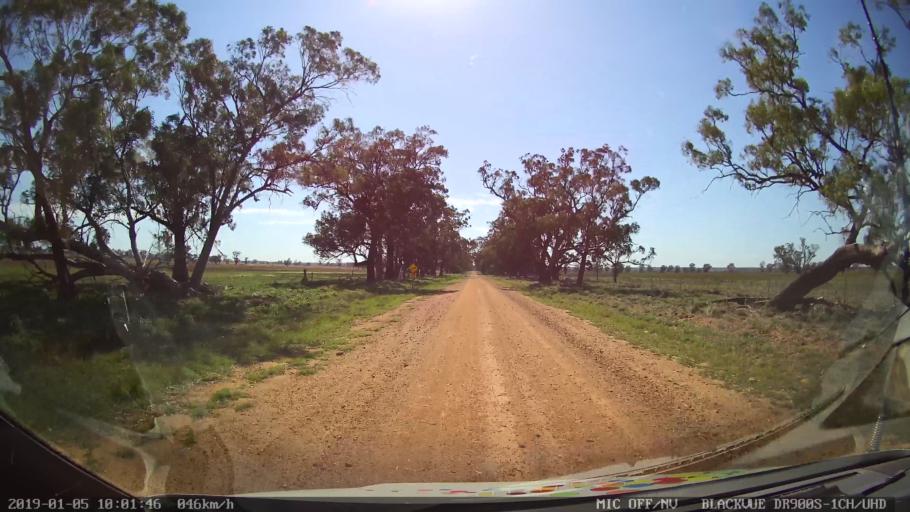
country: AU
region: New South Wales
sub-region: Gilgandra
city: Gilgandra
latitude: -31.6701
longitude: 148.8385
